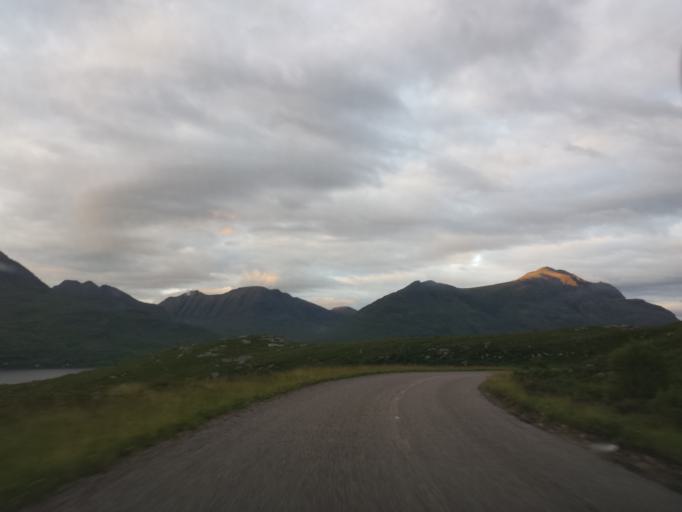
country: GB
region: Scotland
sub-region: Highland
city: Ullapool
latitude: 57.5312
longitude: -5.6088
